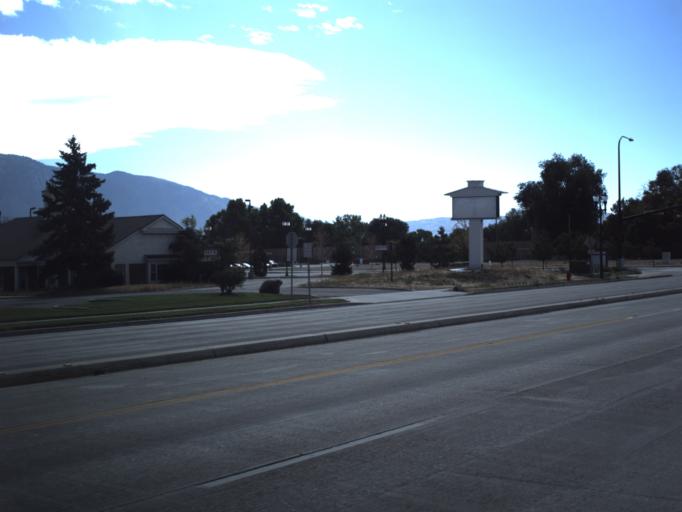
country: US
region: Utah
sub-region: Salt Lake County
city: West Jordan
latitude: 40.6065
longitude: -111.9389
